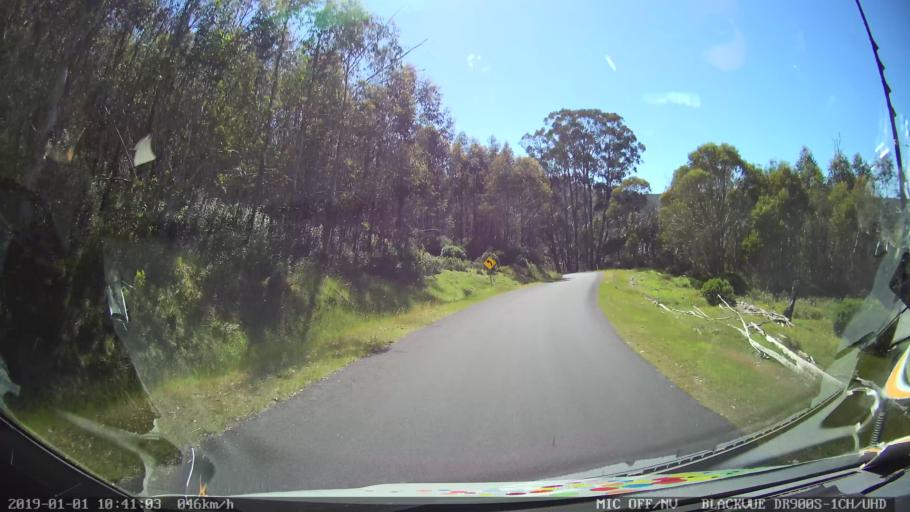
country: AU
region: New South Wales
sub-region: Snowy River
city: Jindabyne
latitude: -36.0369
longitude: 148.3170
